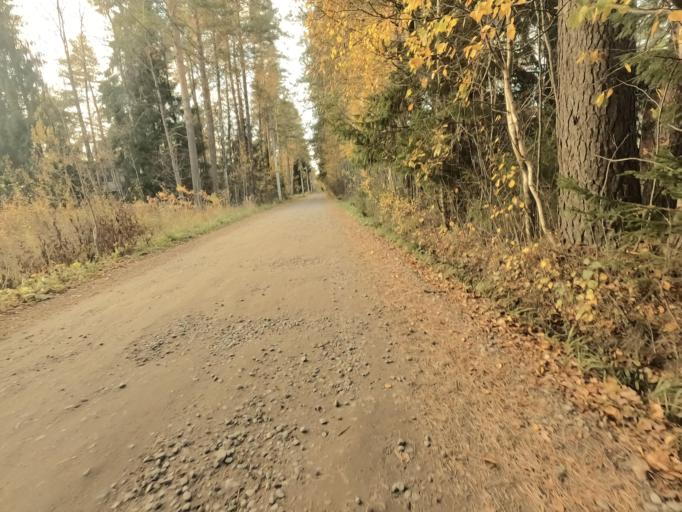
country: RU
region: St.-Petersburg
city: Beloostrov
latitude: 60.1697
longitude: 29.9866
